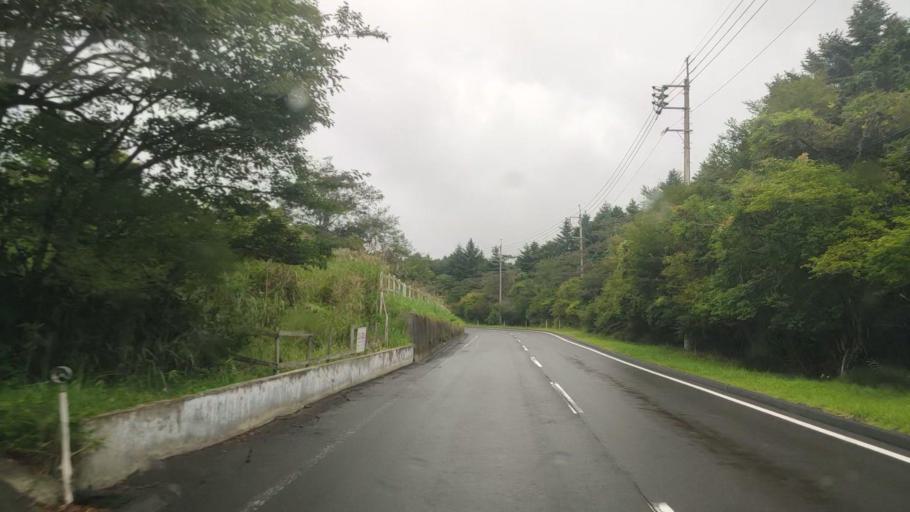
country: JP
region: Shizuoka
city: Fuji
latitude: 35.2818
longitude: 138.7804
